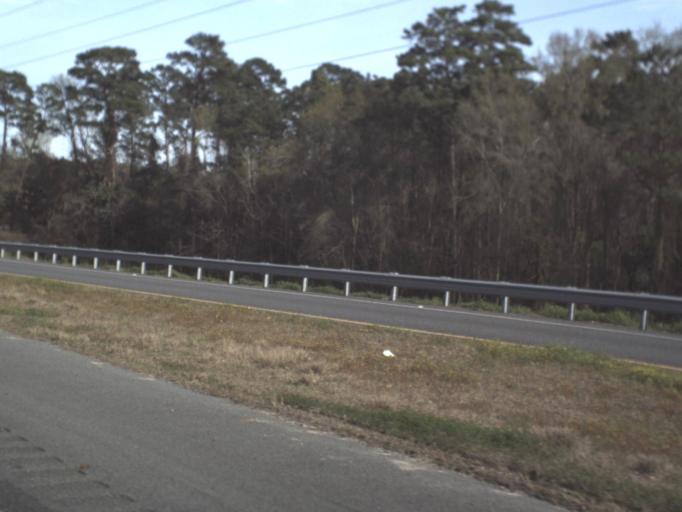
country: US
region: Florida
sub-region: Leon County
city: Tallahassee
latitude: 30.4836
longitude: -84.3043
